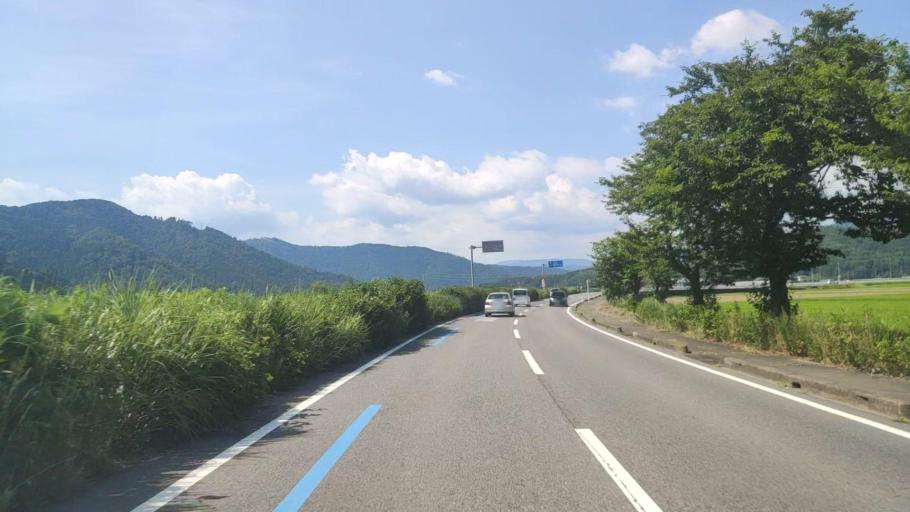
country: JP
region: Shiga Prefecture
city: Nagahama
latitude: 35.4786
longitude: 136.2093
